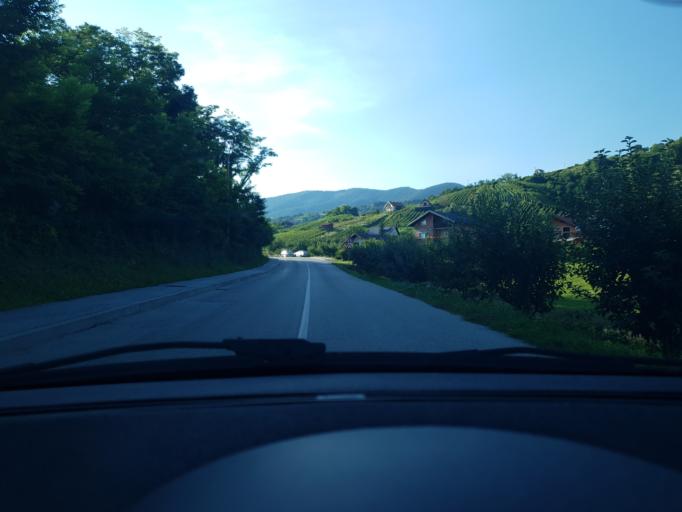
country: HR
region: Krapinsko-Zagorska
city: Radoboj
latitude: 46.1619
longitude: 15.9362
